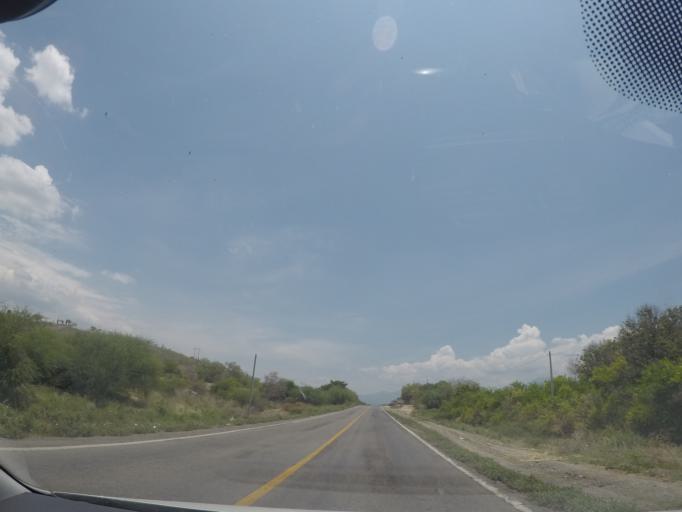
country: MX
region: Oaxaca
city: Santa Maria Jalapa del Marques
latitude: 16.4394
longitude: -95.5031
